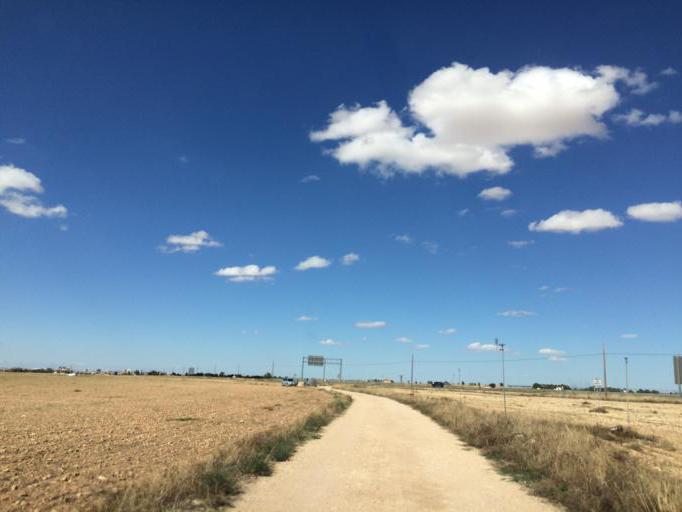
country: ES
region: Castille-La Mancha
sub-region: Provincia de Albacete
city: Albacete
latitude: 38.9439
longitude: -1.8379
